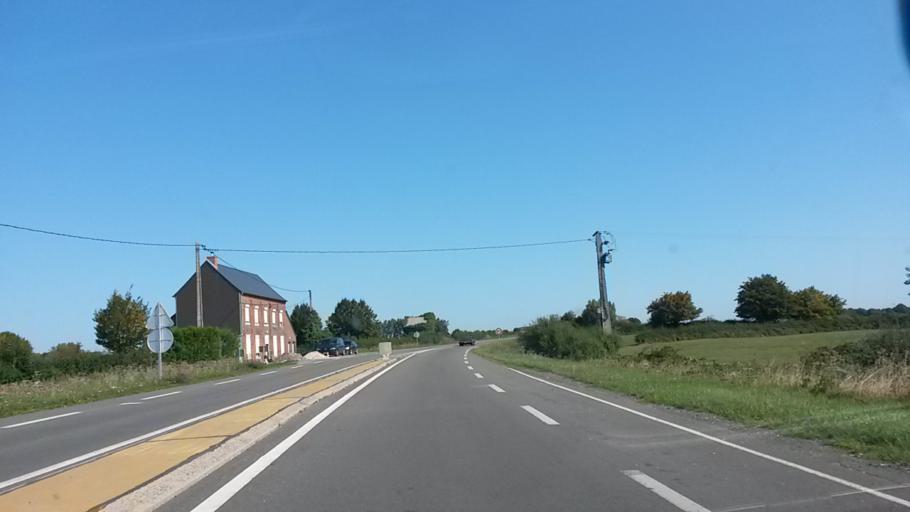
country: FR
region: Nord-Pas-de-Calais
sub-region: Departement du Nord
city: Avesnelles
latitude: 50.1440
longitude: 3.9478
